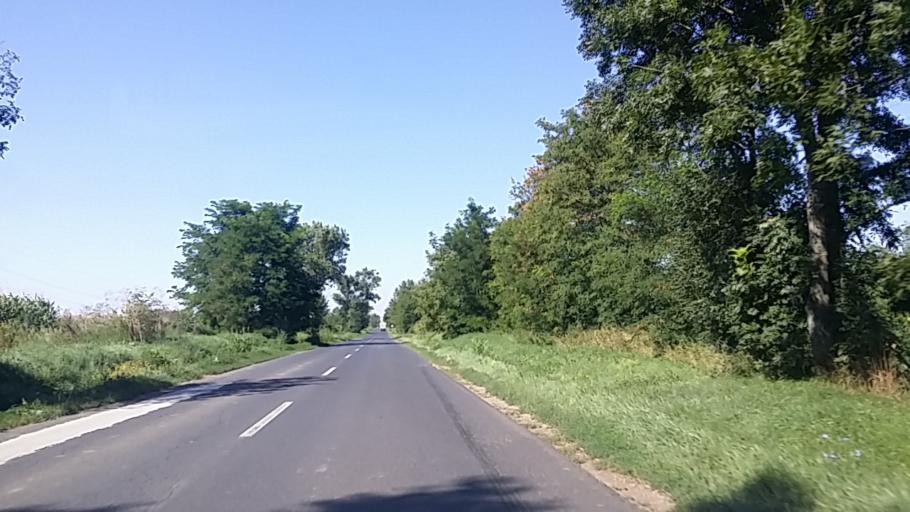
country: HU
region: Fejer
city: Sarbogard
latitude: 46.8716
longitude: 18.6665
